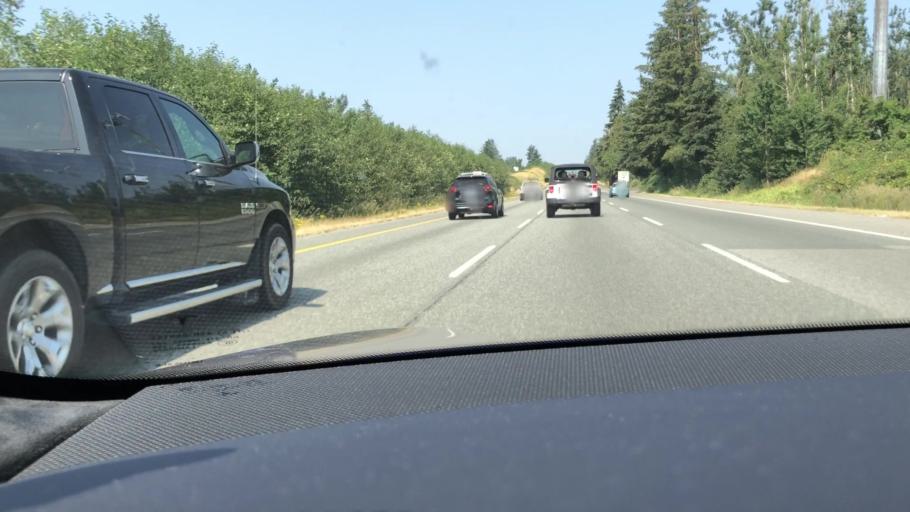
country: CA
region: British Columbia
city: Aldergrove
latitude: 49.0617
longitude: -122.3911
